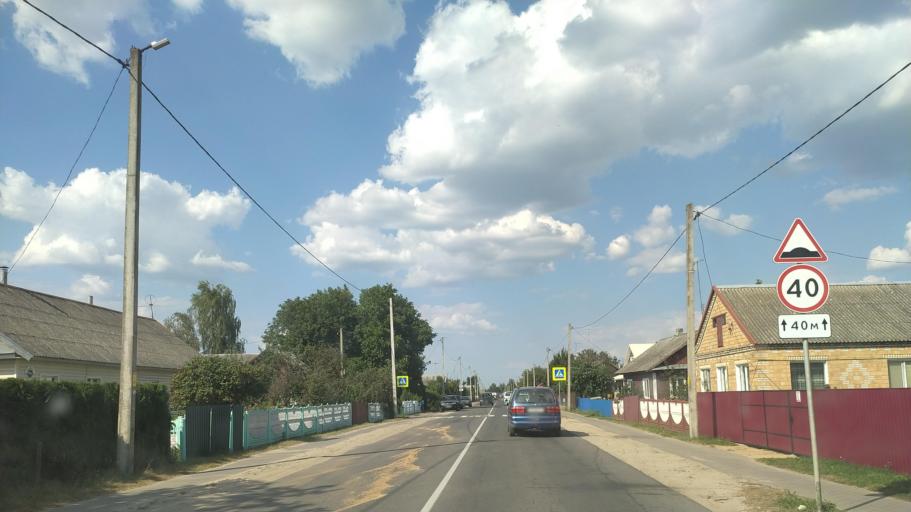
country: BY
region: Brest
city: Drahichyn
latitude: 52.1944
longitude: 25.1475
